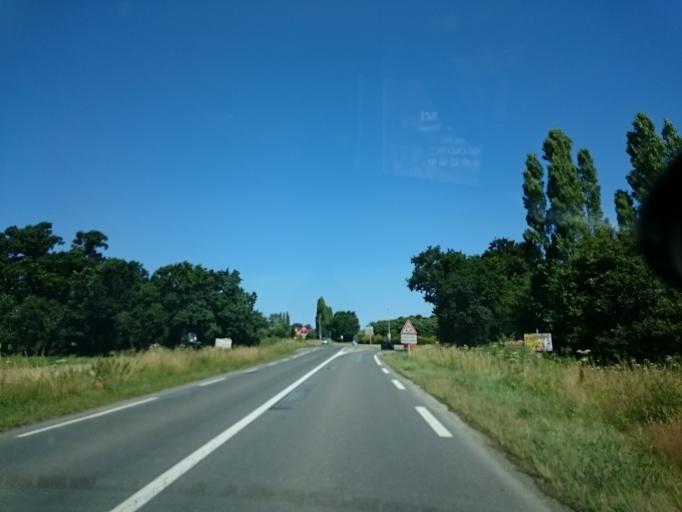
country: FR
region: Brittany
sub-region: Departement d'Ille-et-Vilaine
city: La Gouesniere
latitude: 48.6038
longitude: -1.9007
